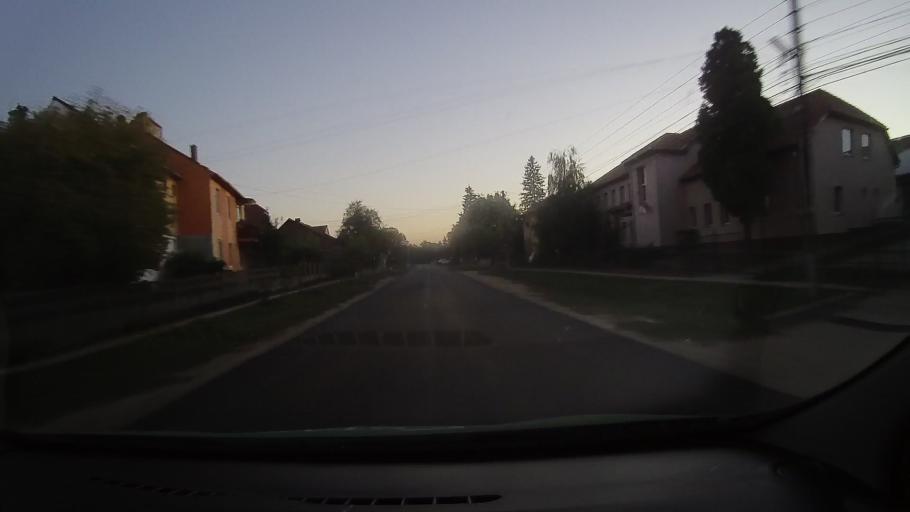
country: RO
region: Bihor
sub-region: Comuna Simian
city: Simian
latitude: 47.4975
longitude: 22.0906
